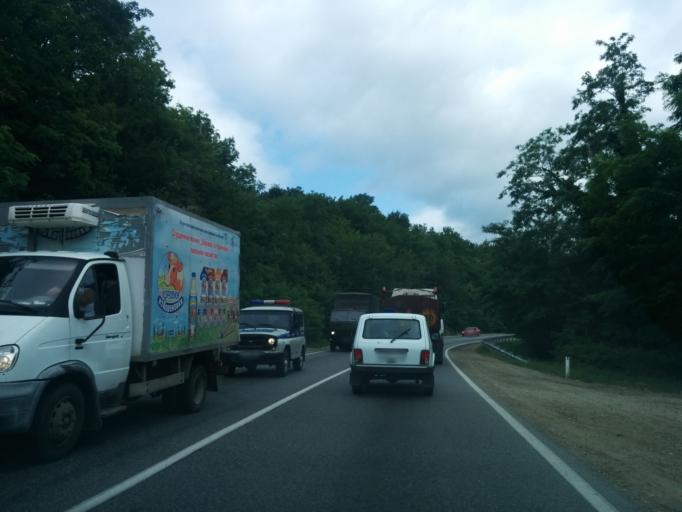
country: RU
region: Krasnodarskiy
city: Agoy
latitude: 44.1243
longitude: 39.0484
